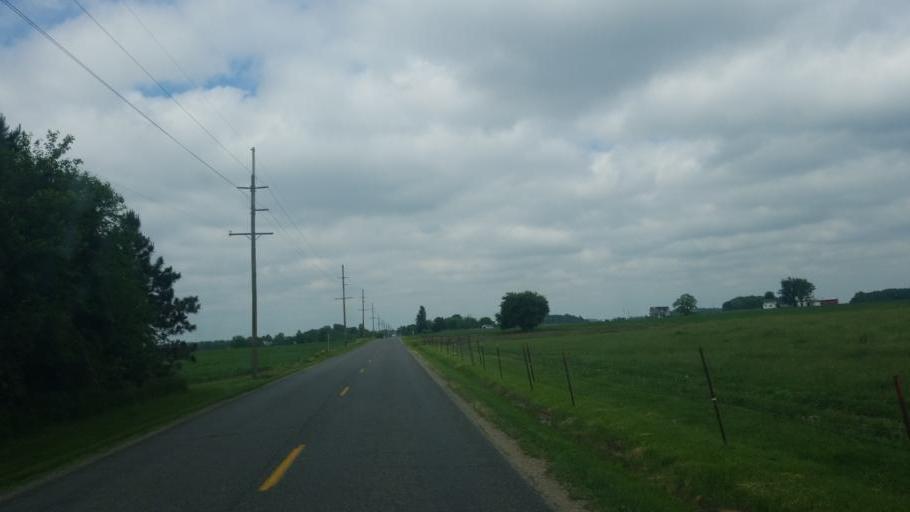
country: US
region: Indiana
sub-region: Elkhart County
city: Nappanee
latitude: 41.4806
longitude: -86.0467
